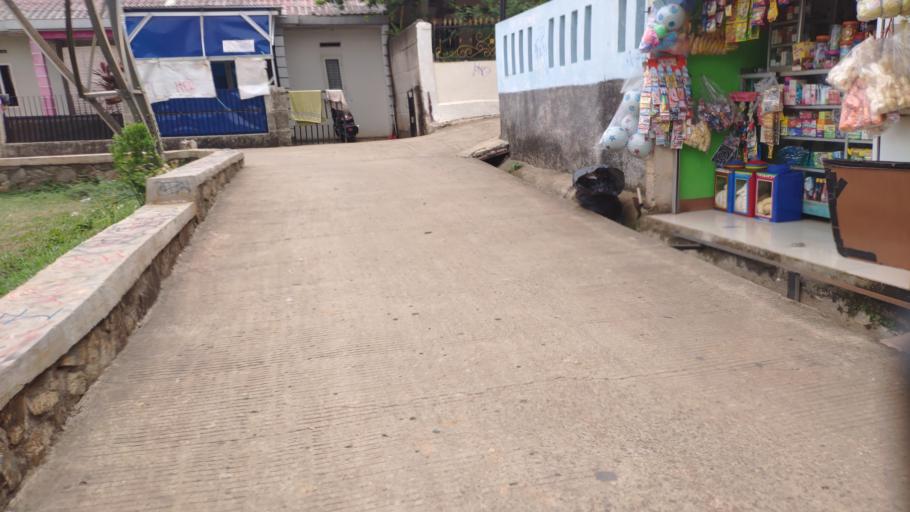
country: ID
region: West Java
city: Sawangan
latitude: -6.3836
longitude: 106.7873
